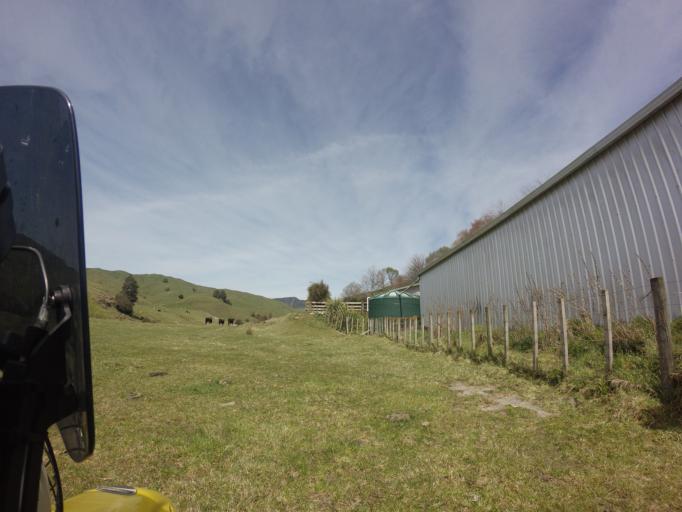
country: NZ
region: Bay of Plenty
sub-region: Opotiki District
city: Opotiki
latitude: -38.4536
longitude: 177.3459
